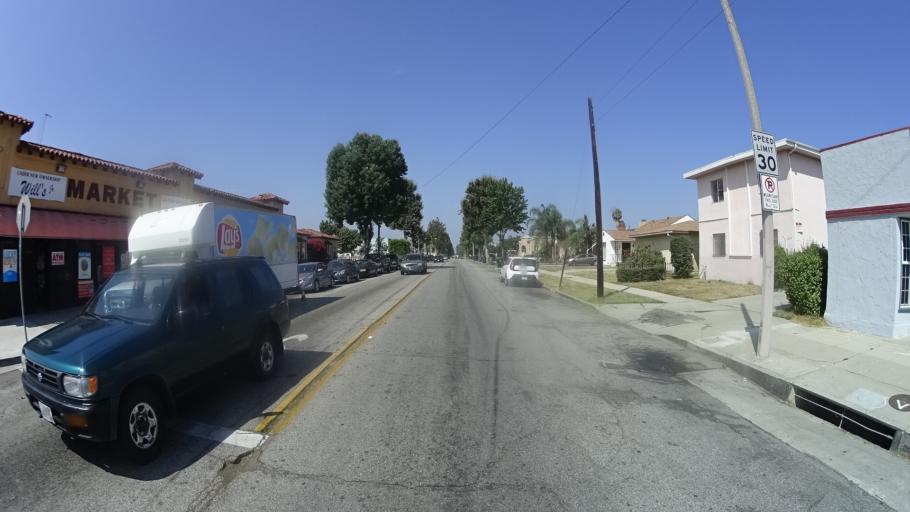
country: US
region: California
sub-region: Los Angeles County
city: View Park-Windsor Hills
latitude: 33.9801
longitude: -118.3384
